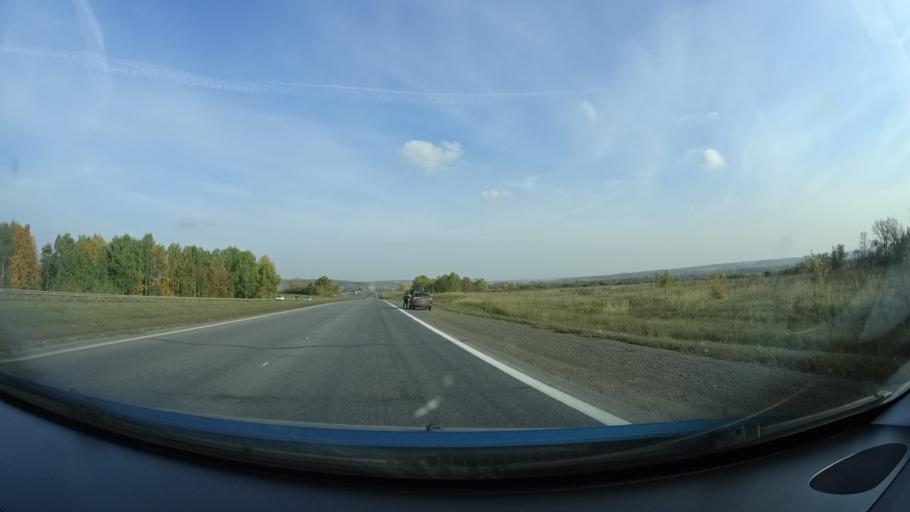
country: RU
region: Bashkortostan
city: Chishmy
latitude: 54.6508
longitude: 55.5148
